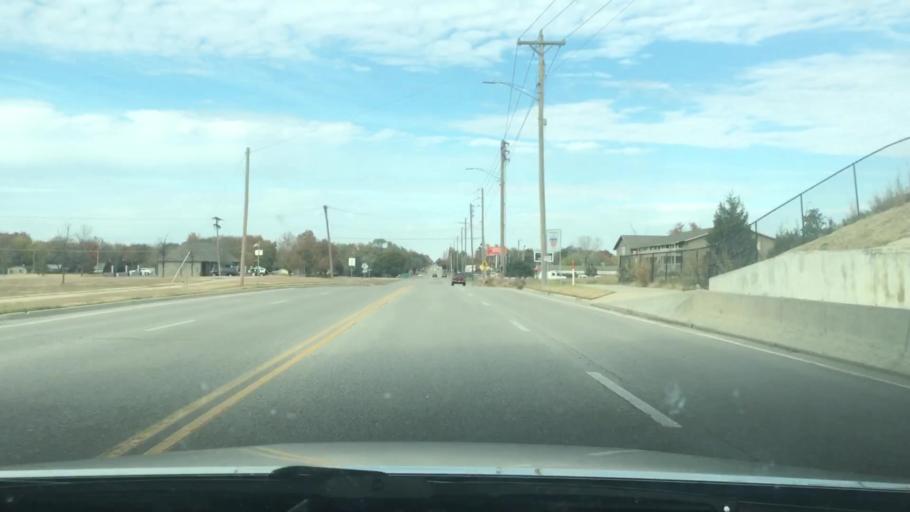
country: US
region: Kansas
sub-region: Sedgwick County
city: Wichita
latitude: 37.6561
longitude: -97.2621
